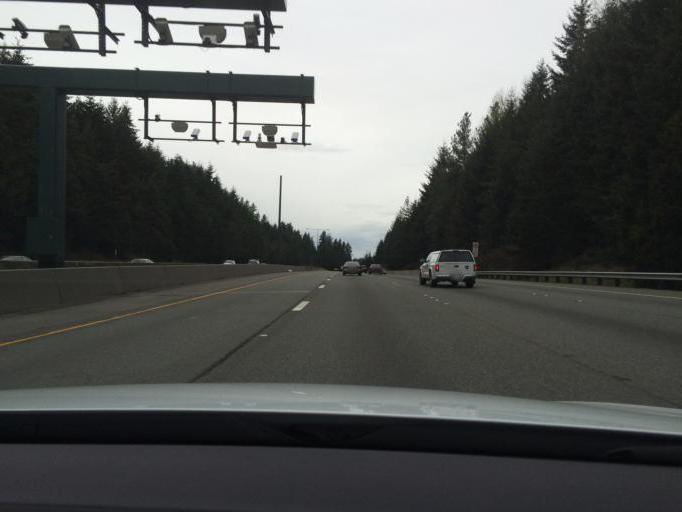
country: US
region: Washington
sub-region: Snohomish County
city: Martha Lake
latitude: 47.8214
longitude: -122.2447
